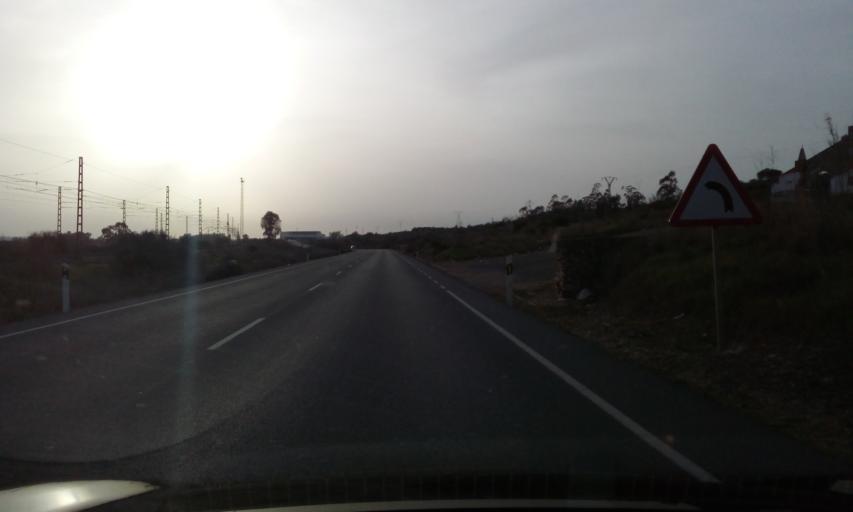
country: ES
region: Andalusia
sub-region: Provincia de Huelva
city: Niebla
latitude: 37.3550
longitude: -6.6950
